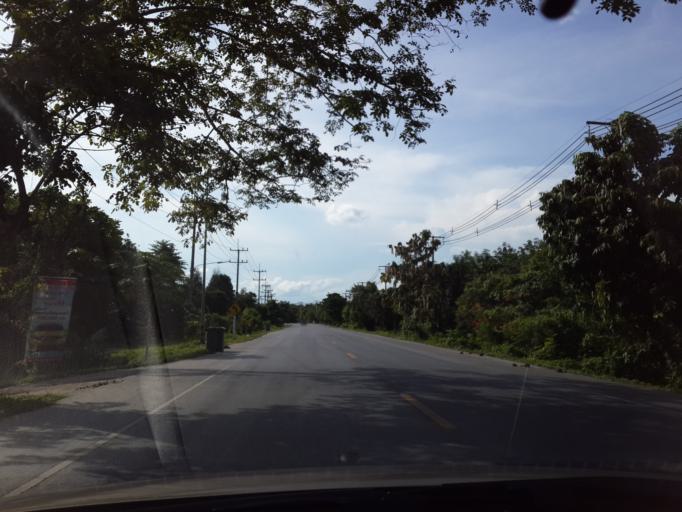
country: TH
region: Yala
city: Yala
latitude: 6.5004
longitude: 101.2783
